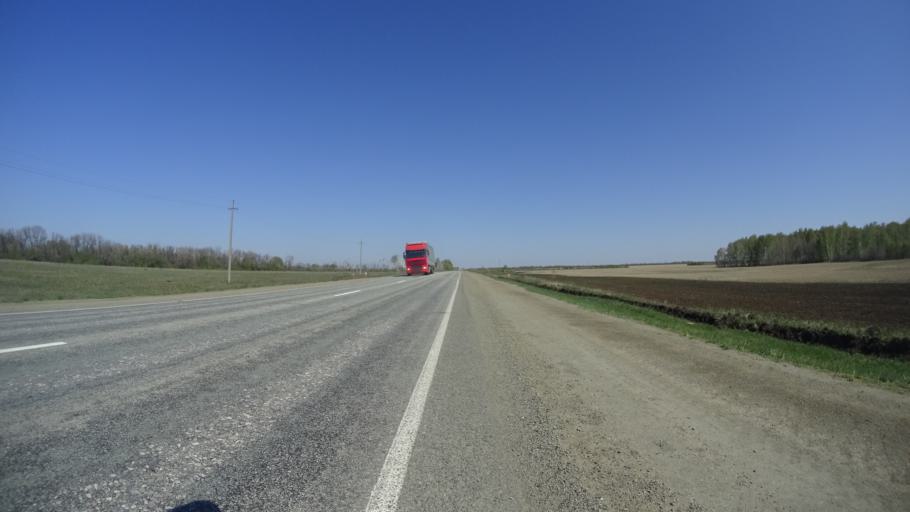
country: RU
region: Chelyabinsk
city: Troitsk
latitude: 54.1918
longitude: 61.4334
